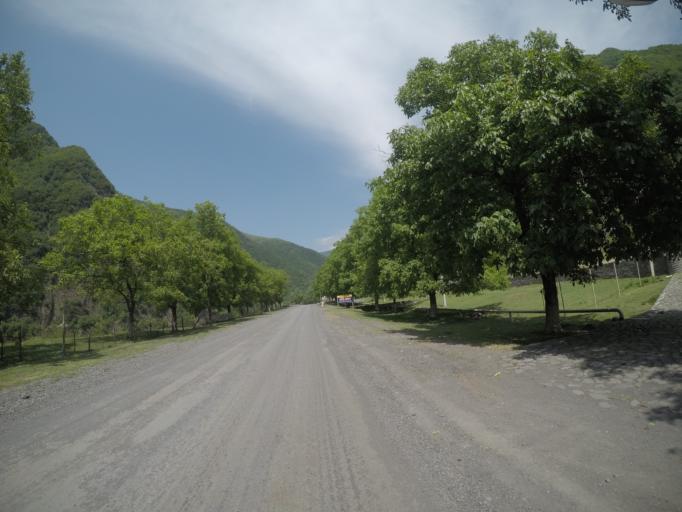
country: AZ
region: Qakh Rayon
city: Qaxbas
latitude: 41.4607
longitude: 47.0289
